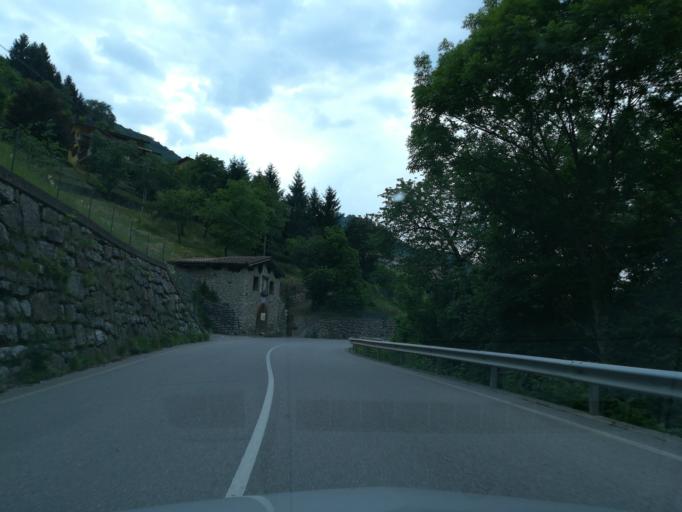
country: IT
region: Lombardy
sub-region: Provincia di Bergamo
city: Strozza
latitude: 45.7693
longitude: 9.5818
